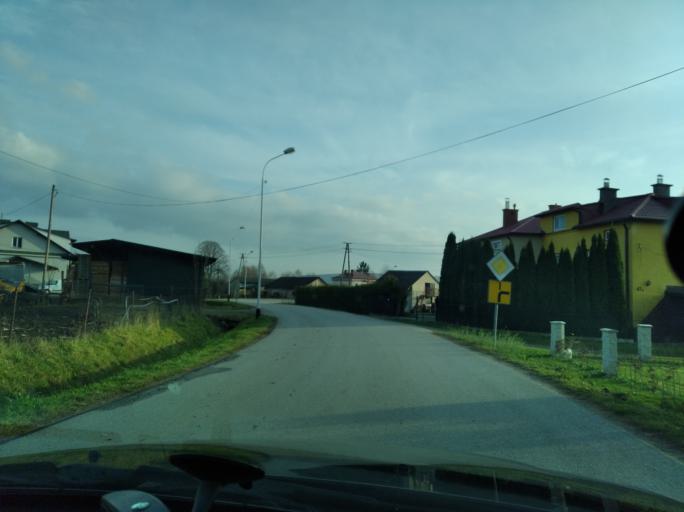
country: PL
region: Subcarpathian Voivodeship
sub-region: Powiat przemyski
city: Przedmiescie Dubieckie
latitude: 49.8321
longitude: 22.3724
